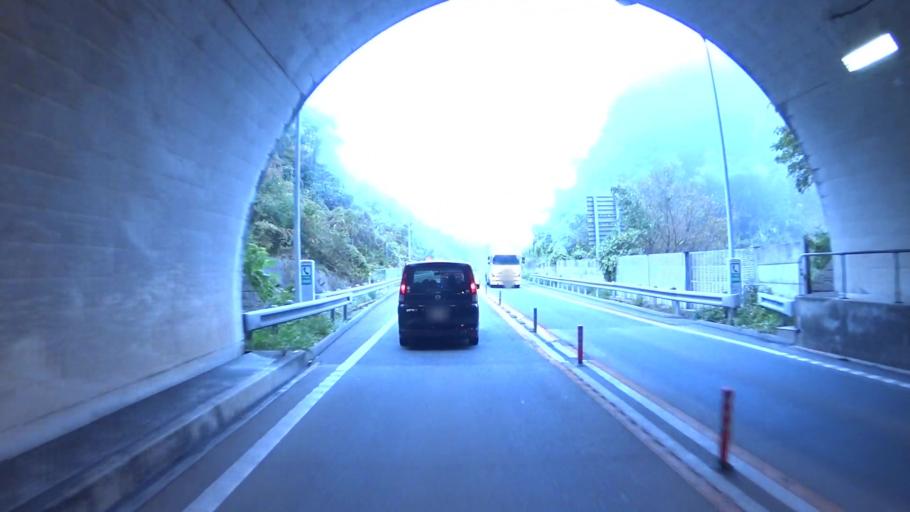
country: JP
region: Kyoto
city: Kameoka
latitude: 35.1276
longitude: 135.4655
